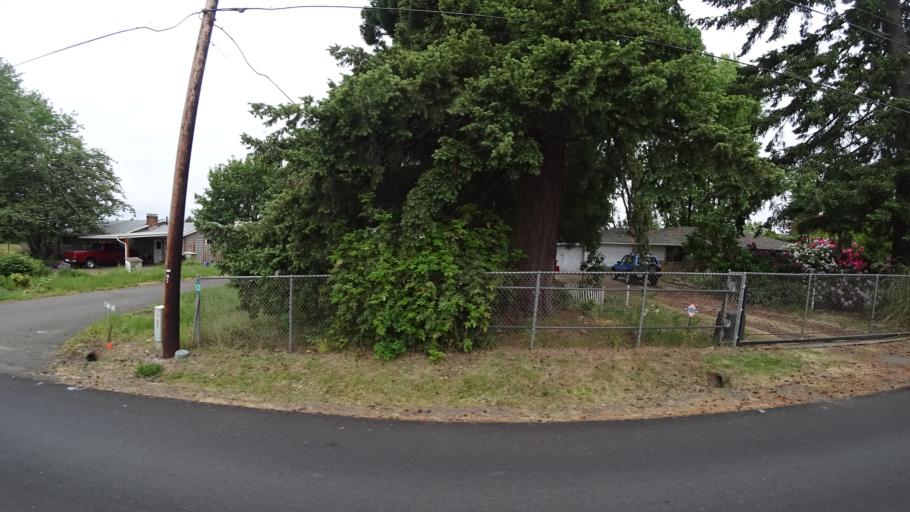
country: US
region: Oregon
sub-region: Washington County
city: Aloha
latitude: 45.4872
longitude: -122.9127
